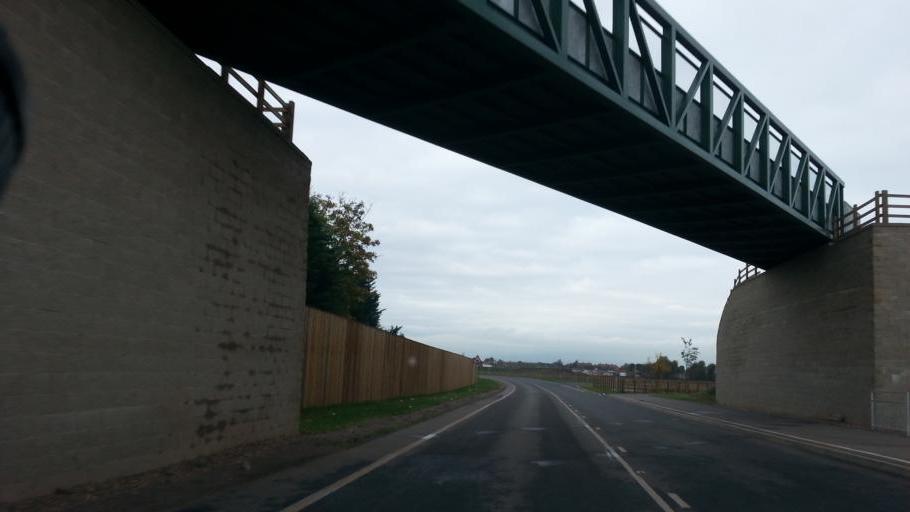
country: GB
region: England
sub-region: Nottinghamshire
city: Newark on Trent
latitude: 53.0505
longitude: -0.8000
